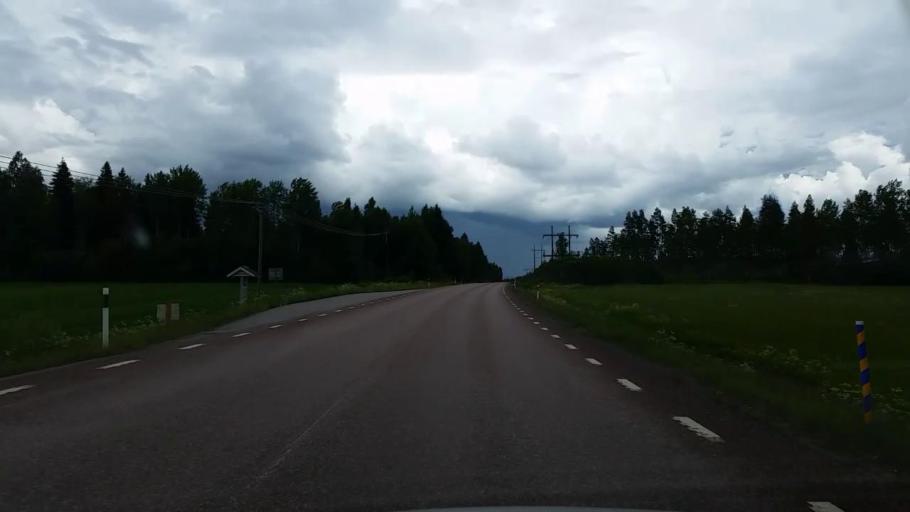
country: SE
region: Gaevleborg
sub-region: Hofors Kommun
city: Hofors
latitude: 60.5172
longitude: 16.4394
